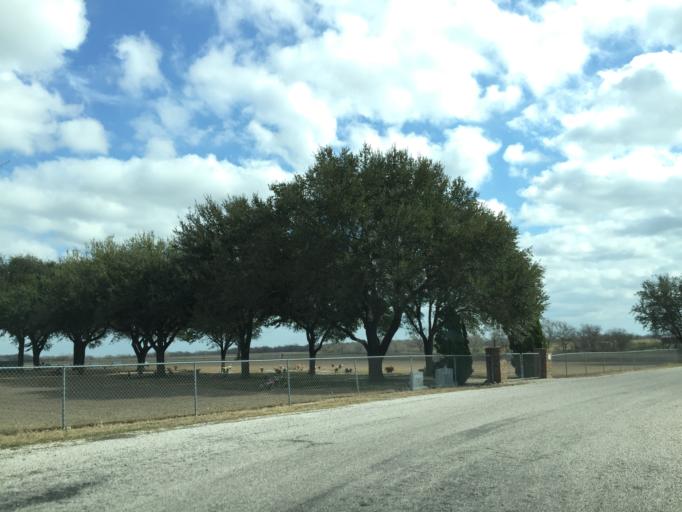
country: US
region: Texas
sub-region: Williamson County
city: Granger
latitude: 30.7116
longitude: -97.4730
